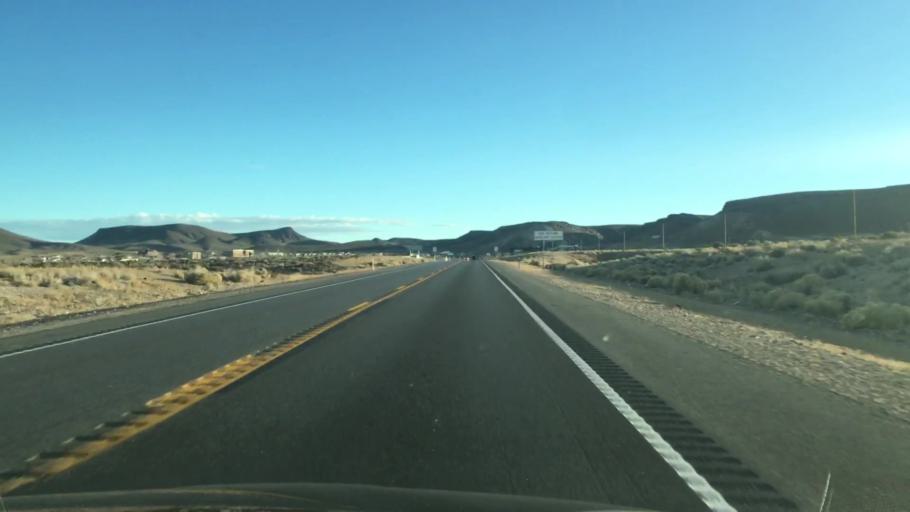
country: US
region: Nevada
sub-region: Esmeralda County
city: Goldfield
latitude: 37.7234
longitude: -117.2435
